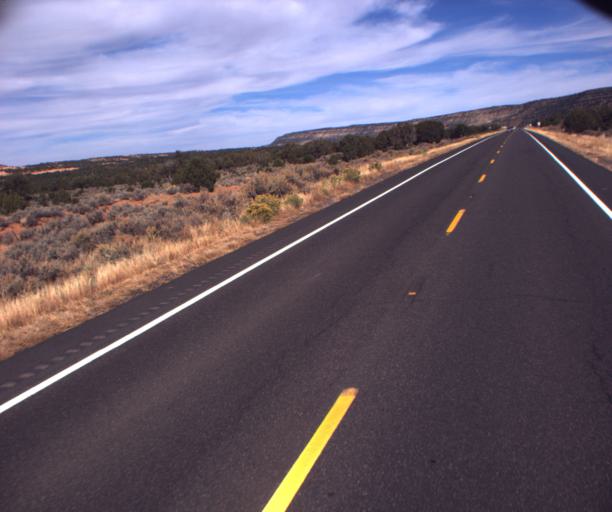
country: US
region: Arizona
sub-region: Navajo County
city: Kayenta
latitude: 36.5579
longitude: -110.5099
